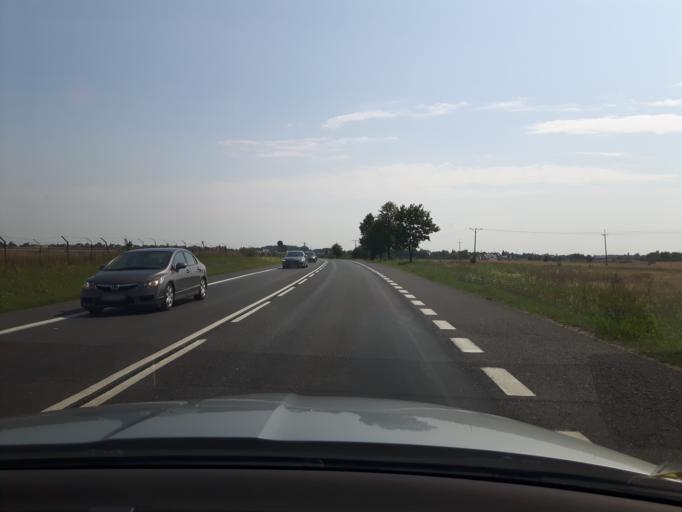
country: PL
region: Masovian Voivodeship
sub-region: Powiat mlawski
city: Mlawa
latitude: 53.1265
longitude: 20.3933
